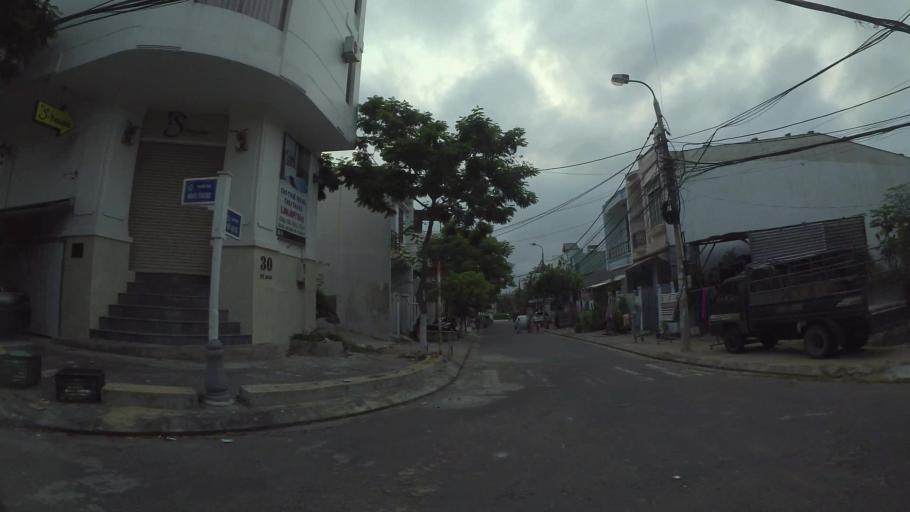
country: VN
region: Da Nang
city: Son Tra
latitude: 16.0408
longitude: 108.2399
